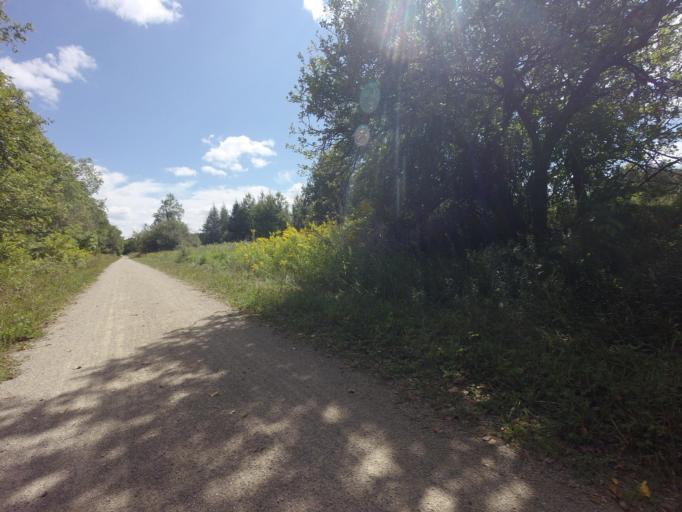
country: CA
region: Ontario
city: Orangeville
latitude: 43.7843
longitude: -80.2301
